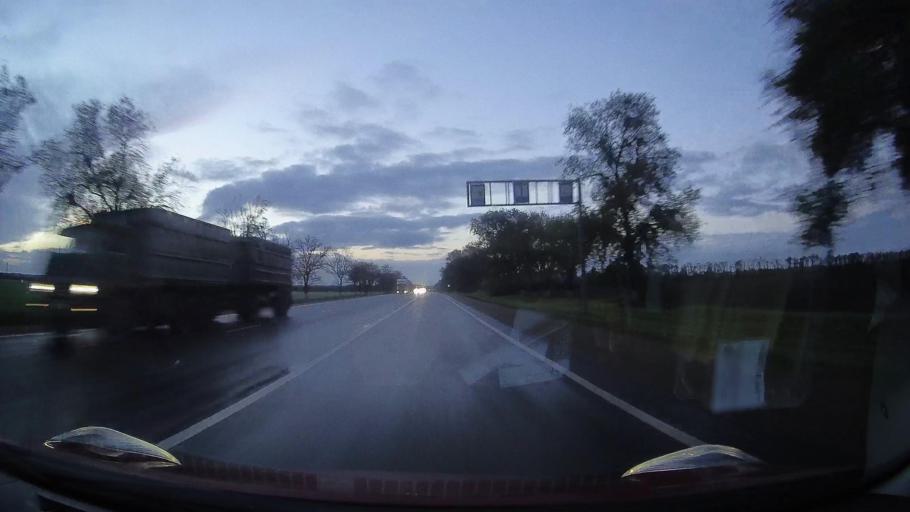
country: RU
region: Krasnodarskiy
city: Zavetnyy
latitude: 44.8927
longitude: 41.2025
